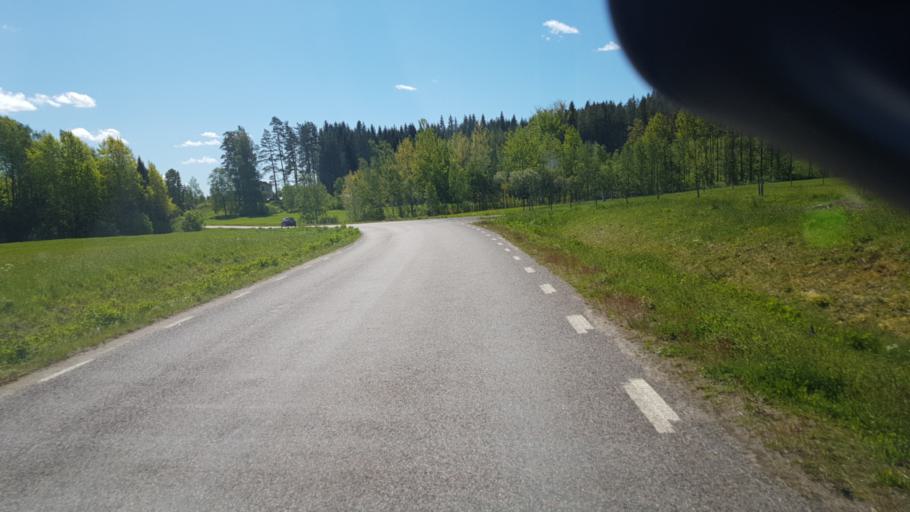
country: SE
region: Vaermland
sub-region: Grums Kommun
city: Slottsbron
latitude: 59.4612
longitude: 12.8767
